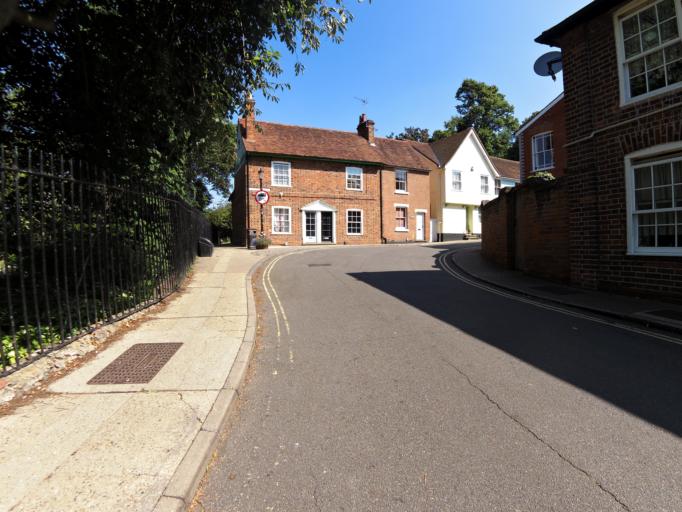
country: GB
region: England
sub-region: Essex
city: Colchester
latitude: 51.8926
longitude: 0.9012
